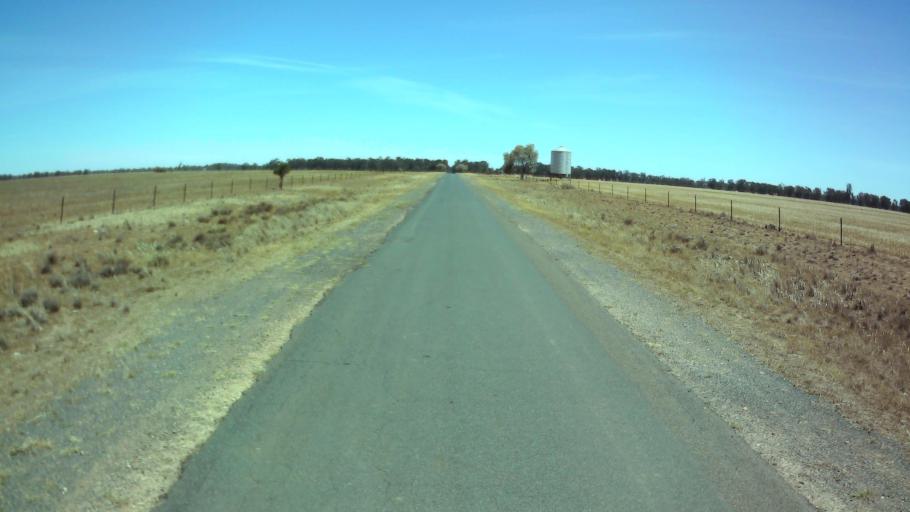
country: AU
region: New South Wales
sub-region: Weddin
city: Grenfell
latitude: -33.8573
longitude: 147.6946
